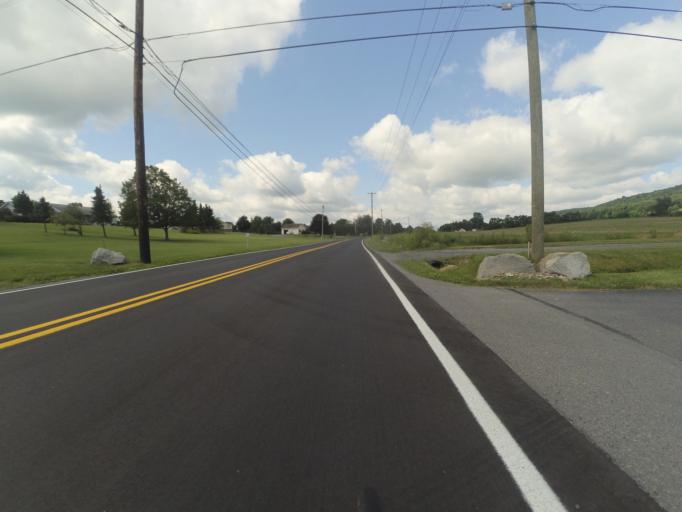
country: US
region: Pennsylvania
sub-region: Centre County
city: Park Forest Village
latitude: 40.8229
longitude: -77.9693
